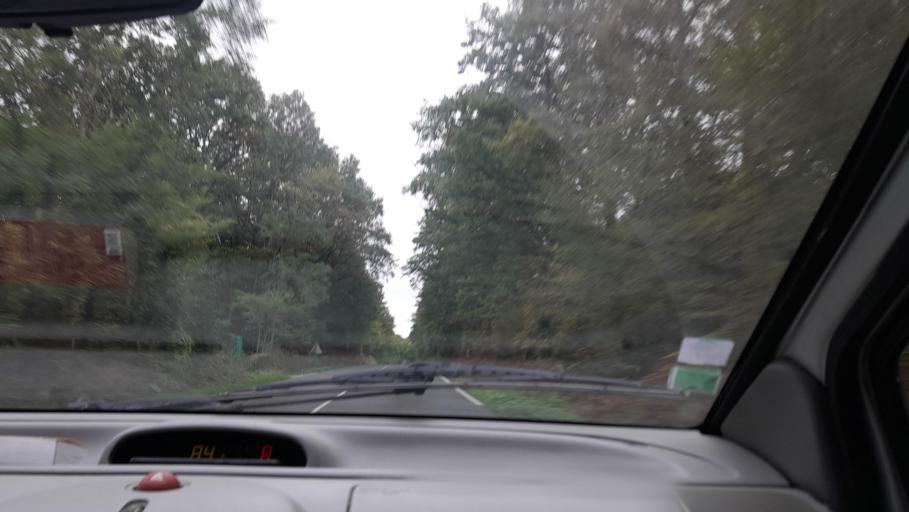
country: FR
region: Pays de la Loire
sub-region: Departement de Maine-et-Loire
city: Pouance
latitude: 47.7022
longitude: -1.1796
